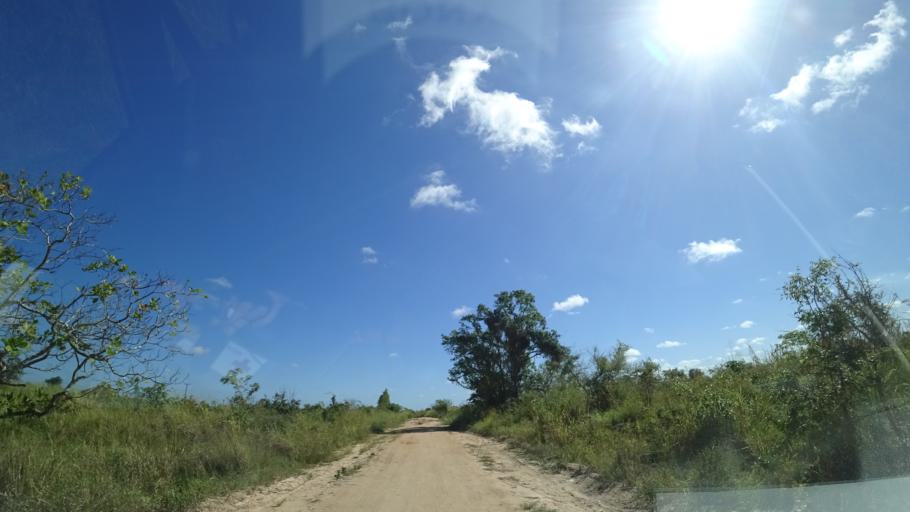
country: MZ
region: Sofala
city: Dondo
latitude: -19.2815
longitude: 34.6843
